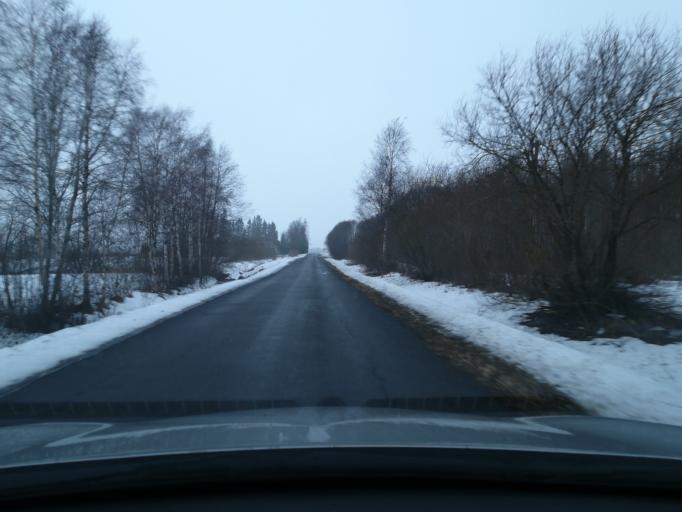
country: EE
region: Harju
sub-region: Raasiku vald
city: Raasiku
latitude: 59.3491
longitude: 25.2114
